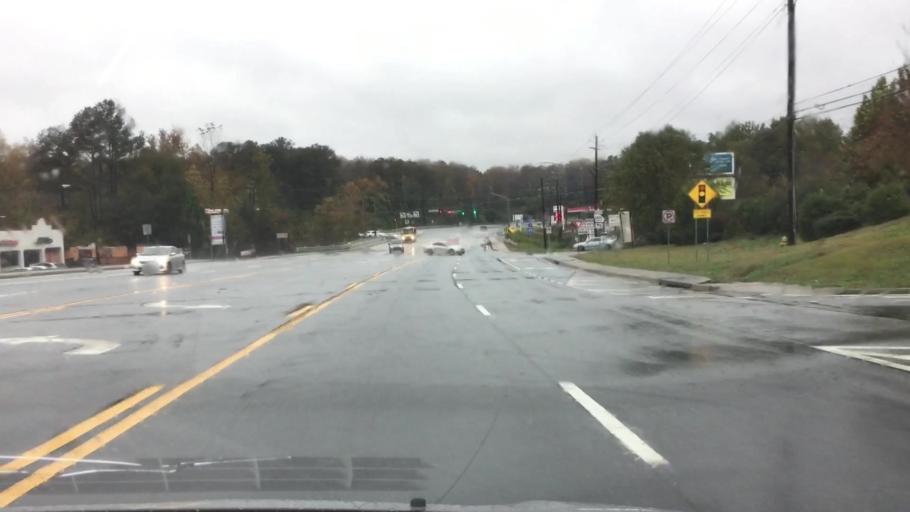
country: US
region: Georgia
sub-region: DeKalb County
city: Panthersville
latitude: 33.6851
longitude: -84.2003
